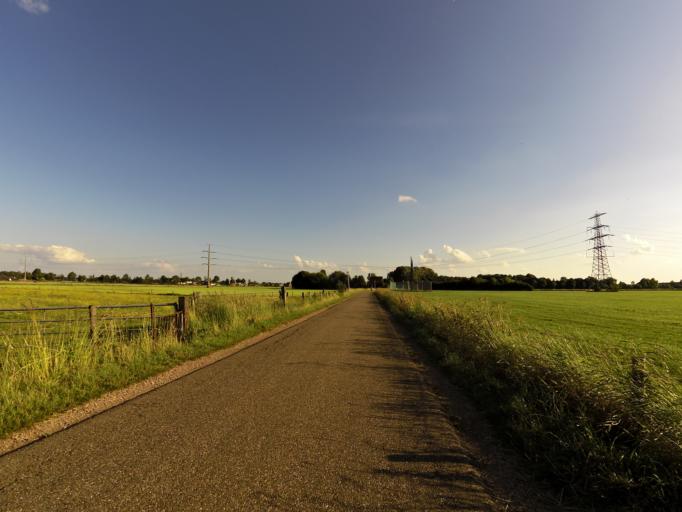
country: NL
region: Gelderland
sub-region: Oude IJsselstreek
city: Gendringen
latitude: 51.9061
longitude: 6.3808
